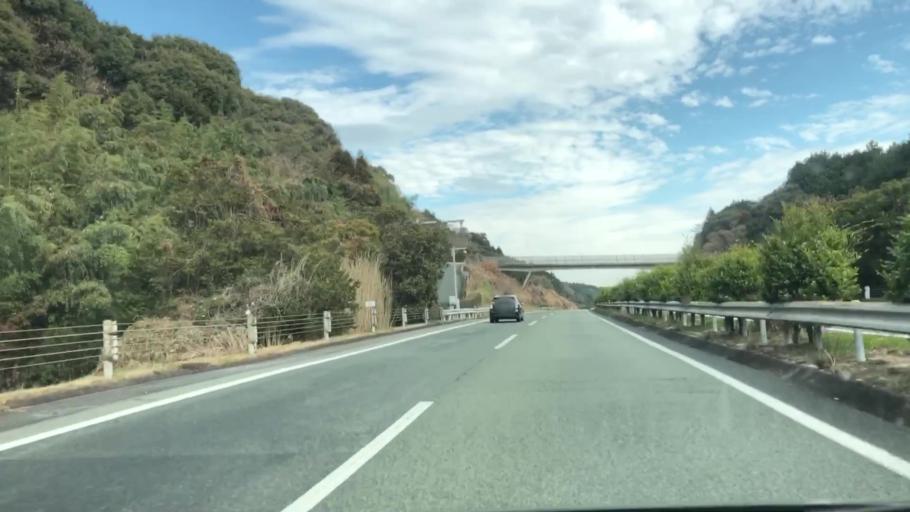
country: JP
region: Saga Prefecture
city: Tosu
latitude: 33.3906
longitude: 130.4894
